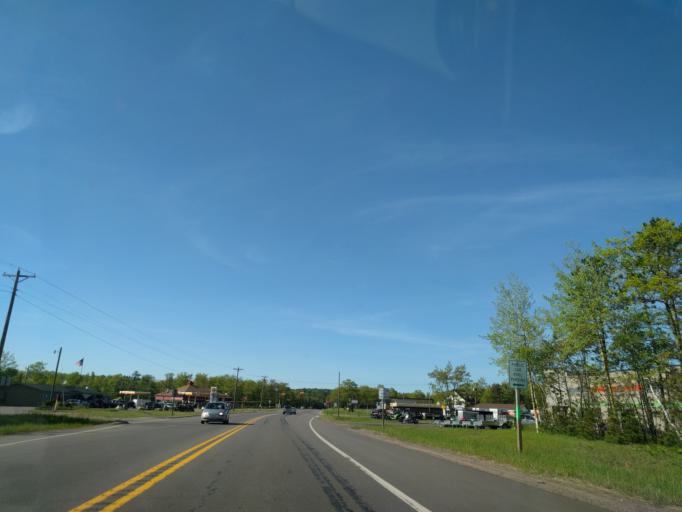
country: US
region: Michigan
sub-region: Marquette County
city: Harvey
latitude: 46.4628
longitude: -87.4255
